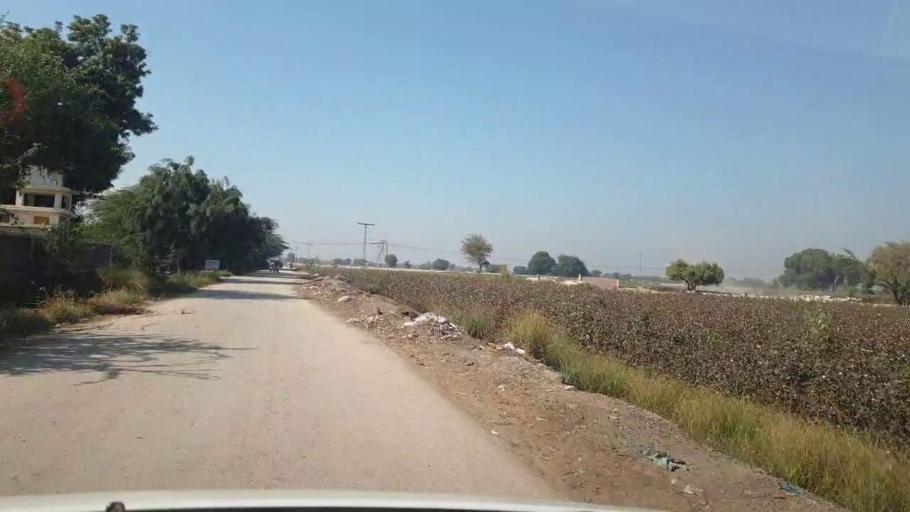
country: PK
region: Sindh
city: Bhan
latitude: 26.6456
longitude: 67.7302
